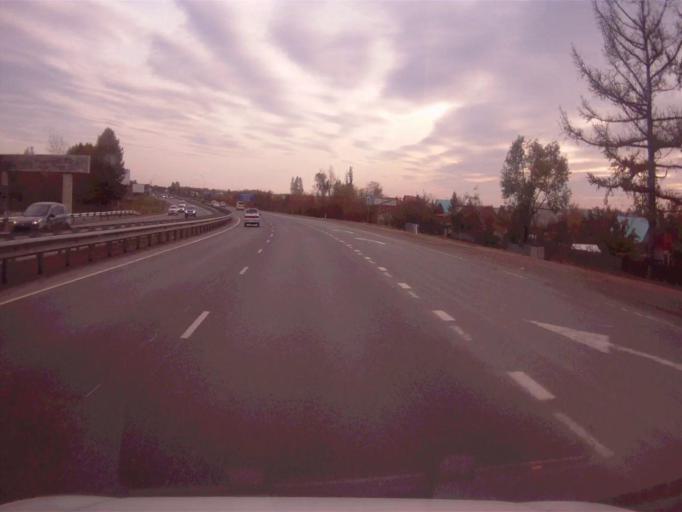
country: RU
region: Chelyabinsk
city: Novosineglazovskiy
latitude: 55.0360
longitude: 61.4418
